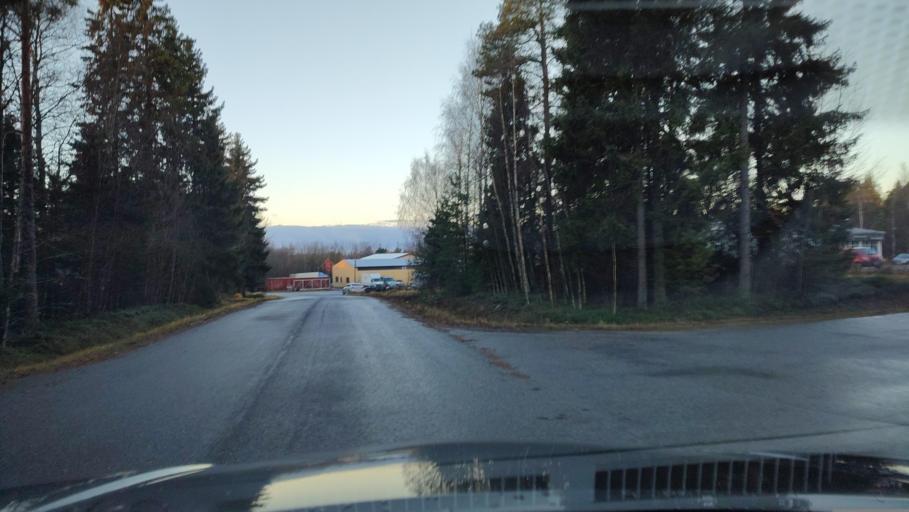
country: FI
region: Ostrobothnia
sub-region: Sydosterbotten
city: Naerpes
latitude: 62.4787
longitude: 21.3699
